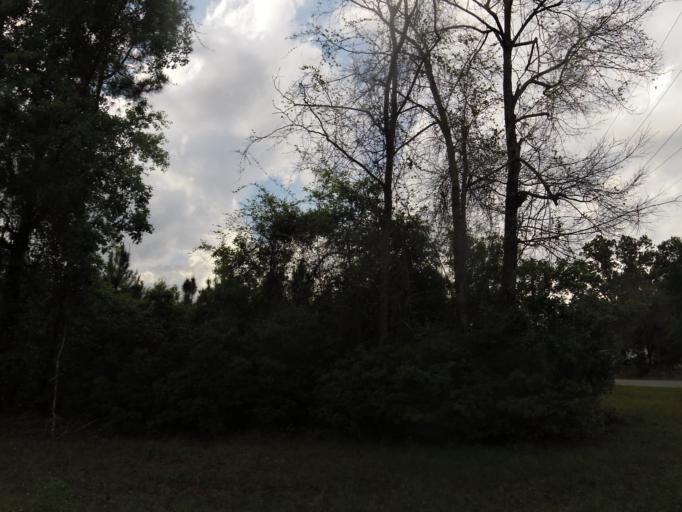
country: US
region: Georgia
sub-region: Charlton County
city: Folkston
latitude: 30.8251
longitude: -82.0407
